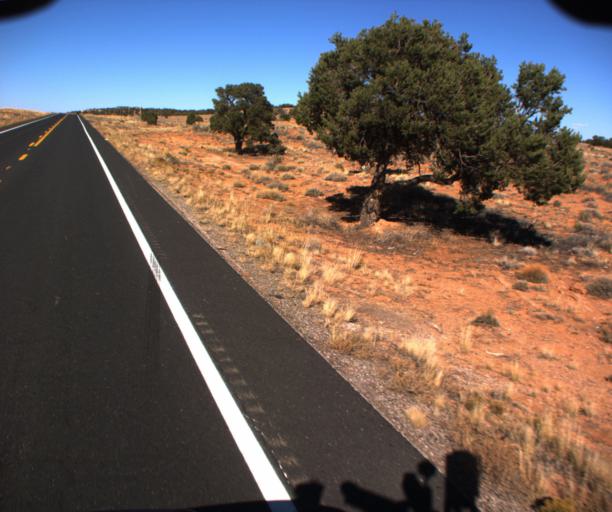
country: US
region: Arizona
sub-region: Coconino County
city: Kaibito
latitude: 36.5144
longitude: -110.7040
